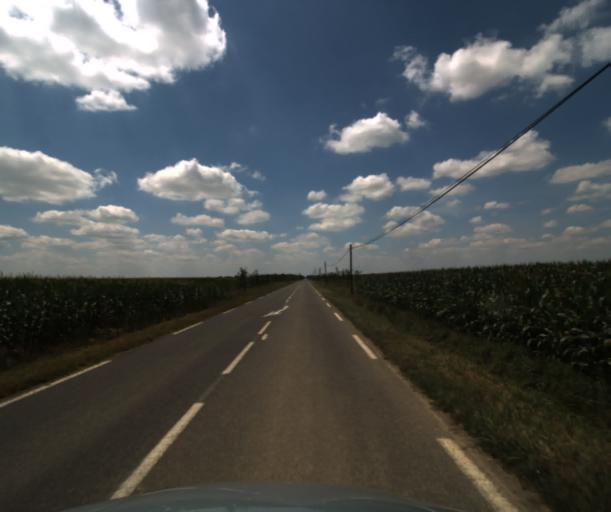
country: FR
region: Midi-Pyrenees
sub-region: Departement de la Haute-Garonne
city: Lherm
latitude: 43.4573
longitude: 1.2033
